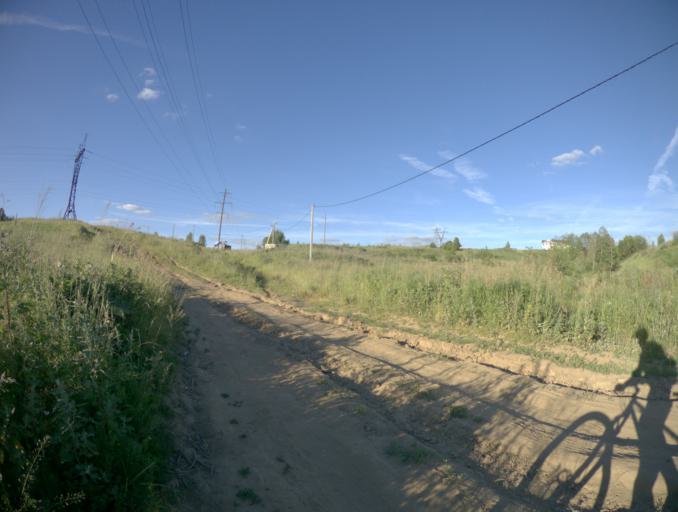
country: RU
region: Vladimir
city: Bogolyubovo
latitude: 56.1849
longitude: 40.5033
